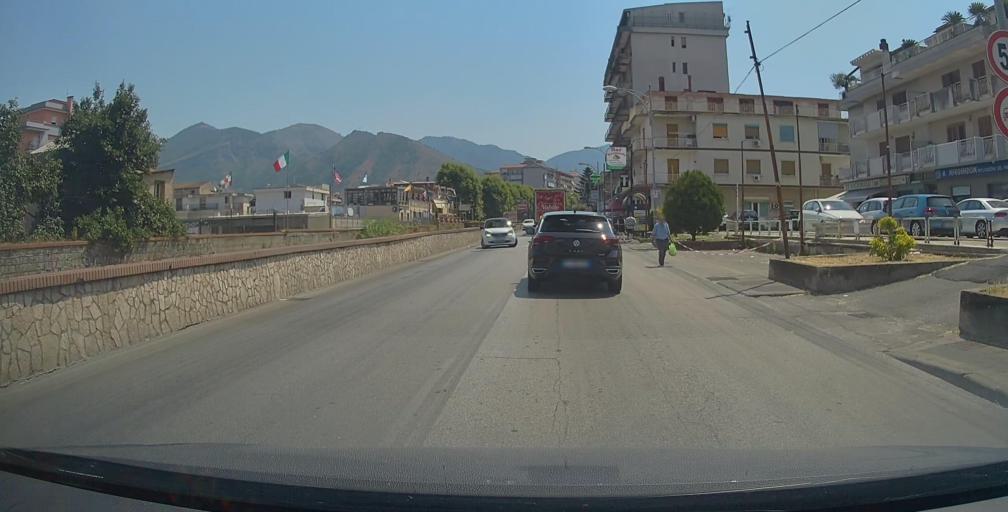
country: IT
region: Campania
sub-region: Provincia di Salerno
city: Nocera Superiore
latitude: 40.7403
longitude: 14.6668
